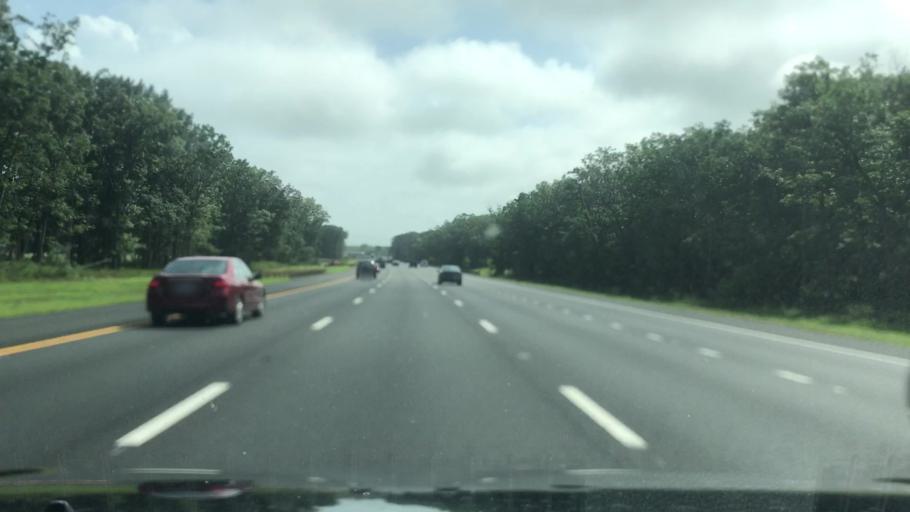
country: US
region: New Jersey
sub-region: Monmouth County
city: Ramtown
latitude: 40.1112
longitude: -74.1342
